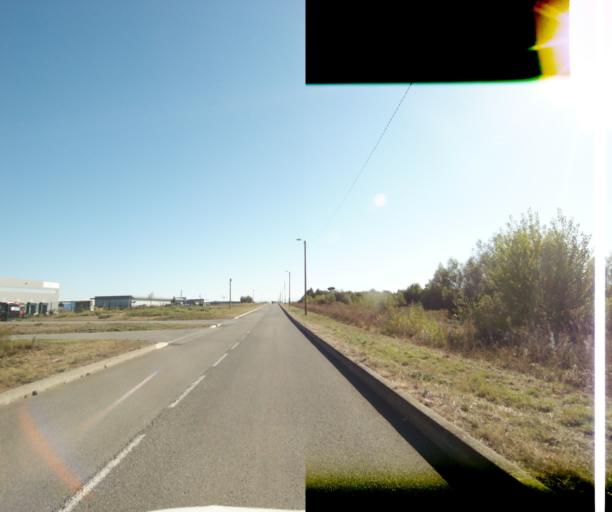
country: FR
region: Auvergne
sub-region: Departement du Puy-de-Dome
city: Gerzat
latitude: 45.8314
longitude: 3.1293
